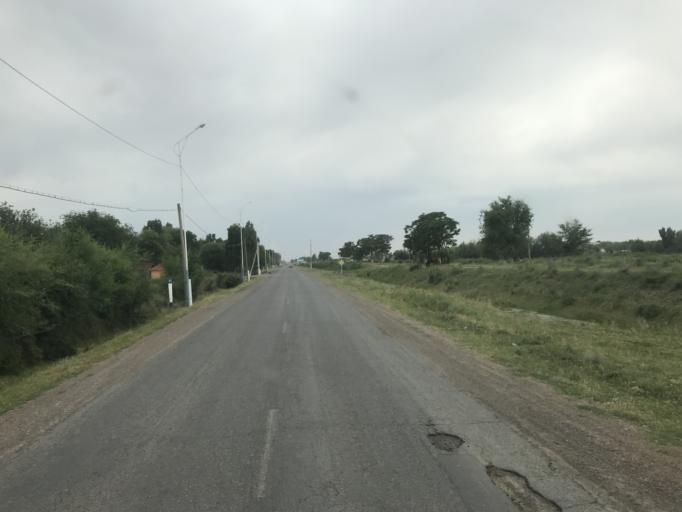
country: KZ
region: Ongtustik Qazaqstan
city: Asykata
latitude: 40.9388
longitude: 68.4128
